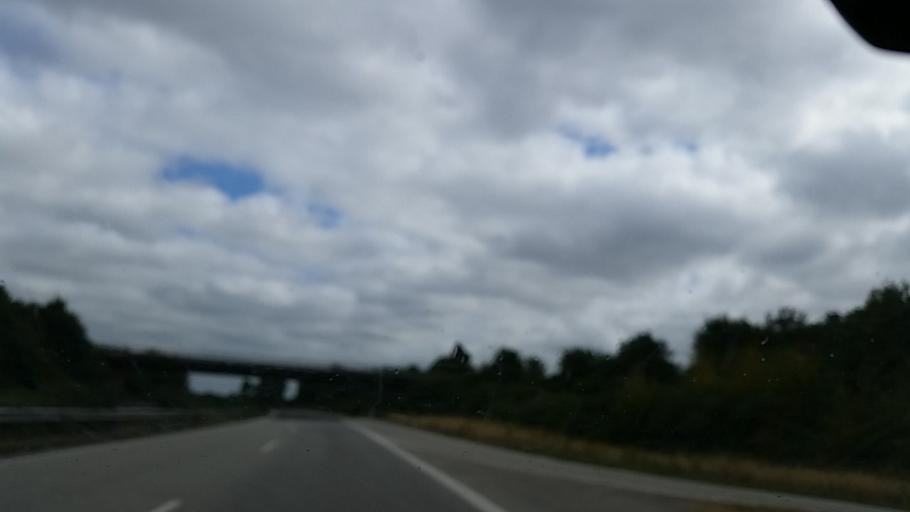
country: DE
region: Schleswig-Holstein
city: Hogersdorf
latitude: 53.8983
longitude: 10.2774
